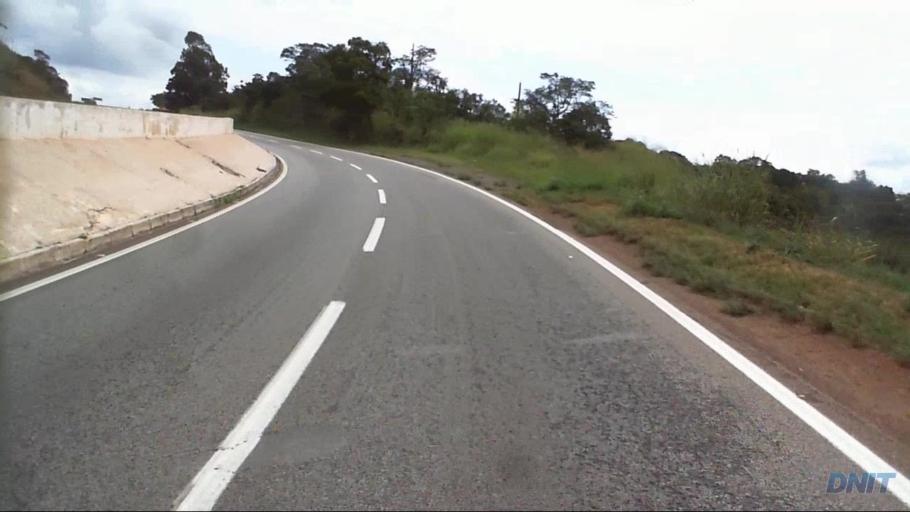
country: BR
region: Minas Gerais
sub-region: Caete
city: Caete
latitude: -19.7874
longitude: -43.6826
